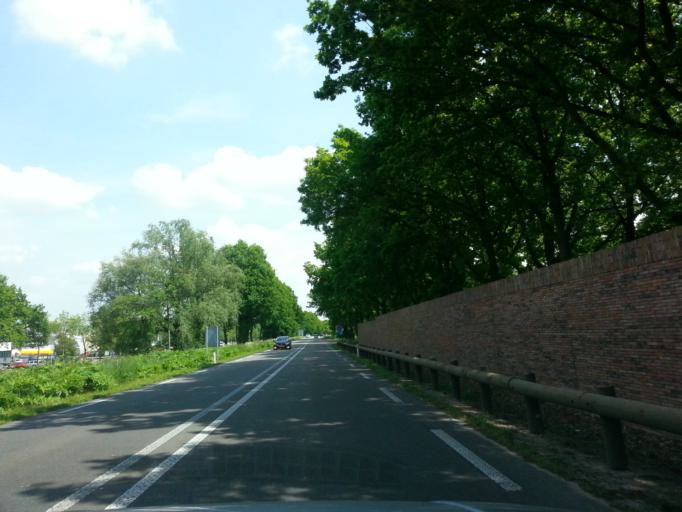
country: NL
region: Gelderland
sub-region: Gemeente Doesburg
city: Doesburg
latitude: 52.0182
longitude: 6.1361
